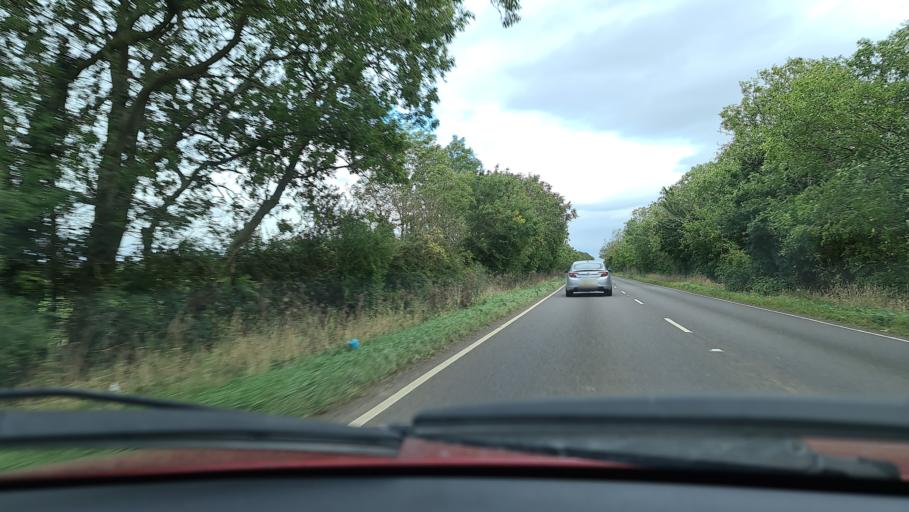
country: GB
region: England
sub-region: Oxfordshire
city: Somerton
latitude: 51.9610
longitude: -1.2103
